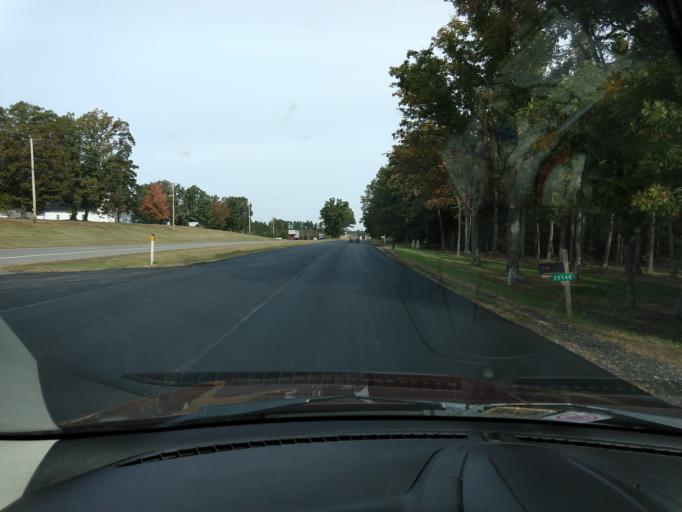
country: US
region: Virginia
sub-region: Pittsylvania County
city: Chatham
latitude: 36.8733
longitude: -79.4092
